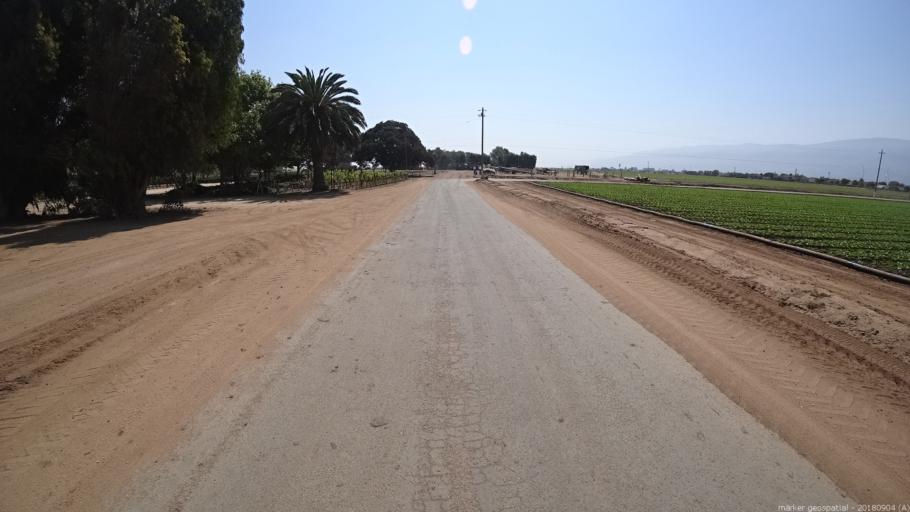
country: US
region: California
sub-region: Monterey County
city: Gonzales
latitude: 36.5283
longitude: -121.4431
